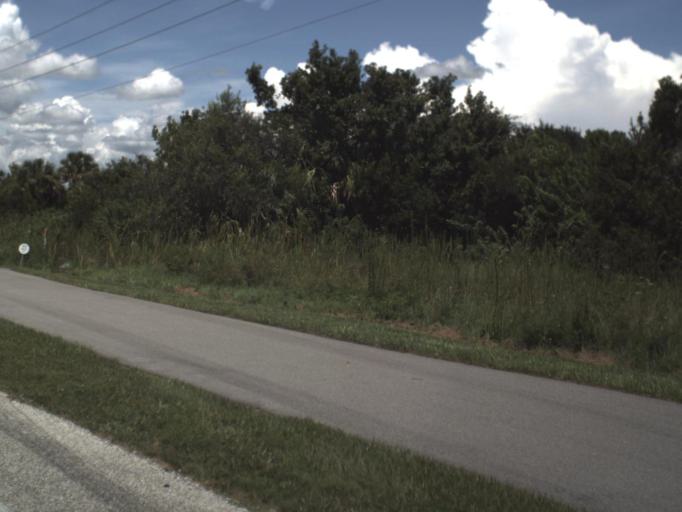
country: US
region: Florida
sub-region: Charlotte County
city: Charlotte Park
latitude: 26.8984
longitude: -82.0303
